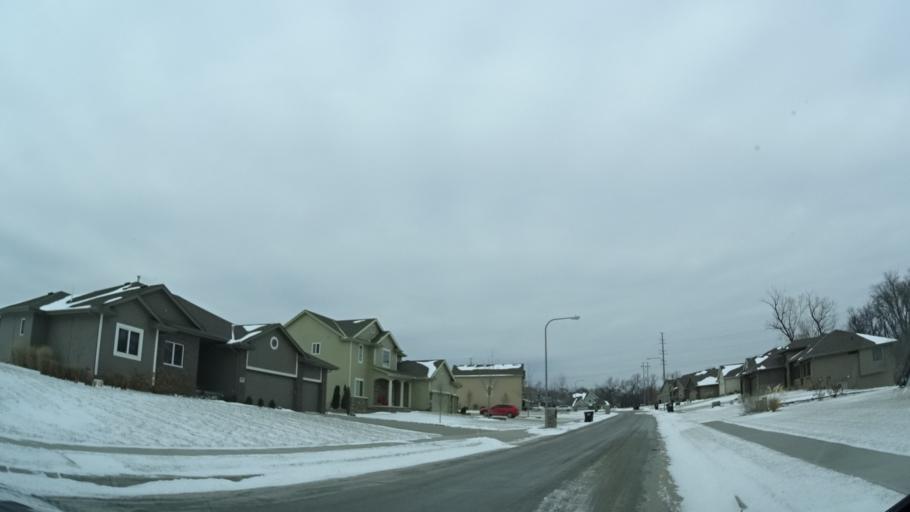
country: US
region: Nebraska
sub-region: Sarpy County
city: Offutt Air Force Base
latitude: 41.1673
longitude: -95.9445
